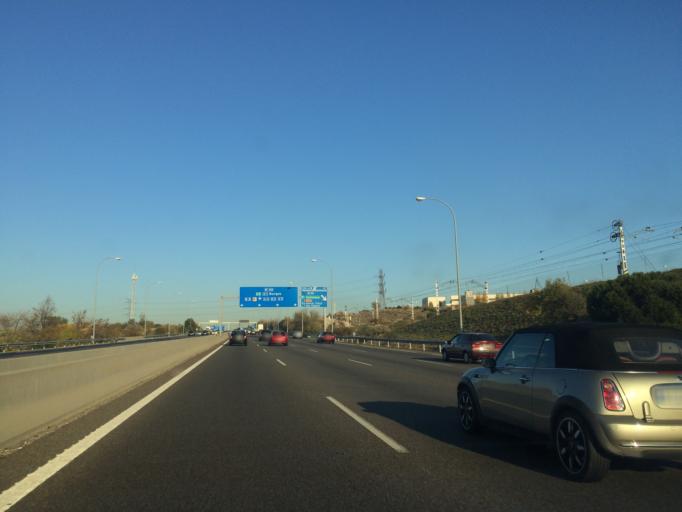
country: ES
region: Madrid
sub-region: Provincia de Madrid
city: Las Tablas
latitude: 40.5105
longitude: -3.7029
